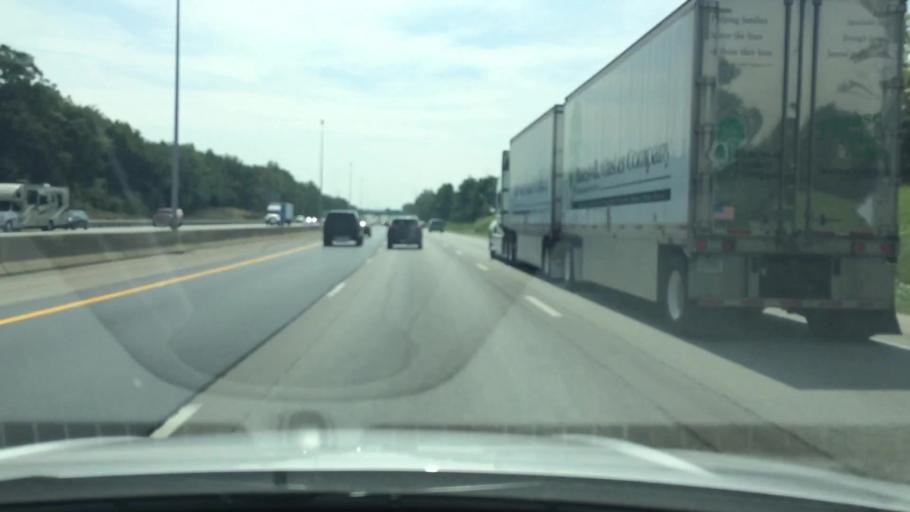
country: US
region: Kentucky
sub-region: Fayette County
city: Lexington-Fayette
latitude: 38.0708
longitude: -84.4509
